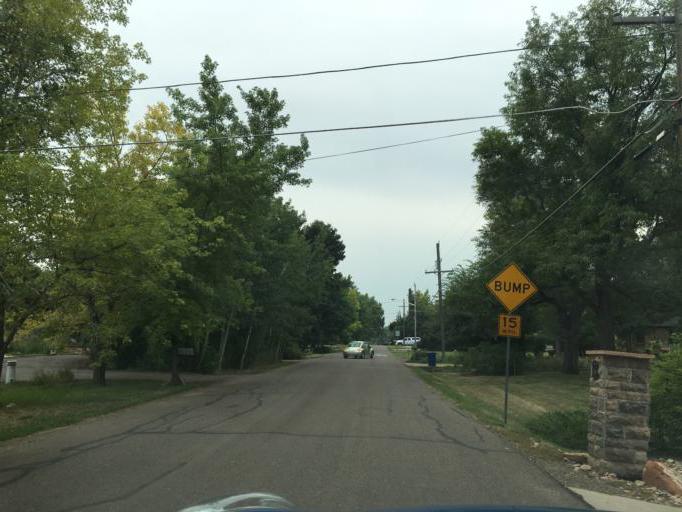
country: US
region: Colorado
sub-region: Jefferson County
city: Wheat Ridge
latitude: 39.7452
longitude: -105.1014
